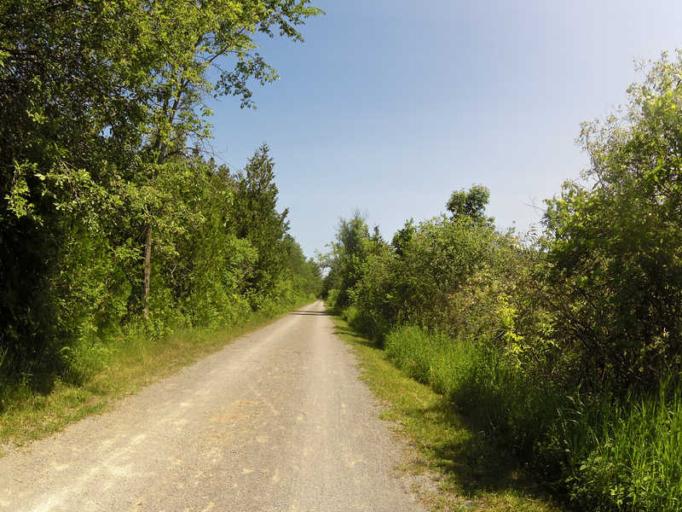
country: CA
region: Ontario
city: Peterborough
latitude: 44.3673
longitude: -78.2874
